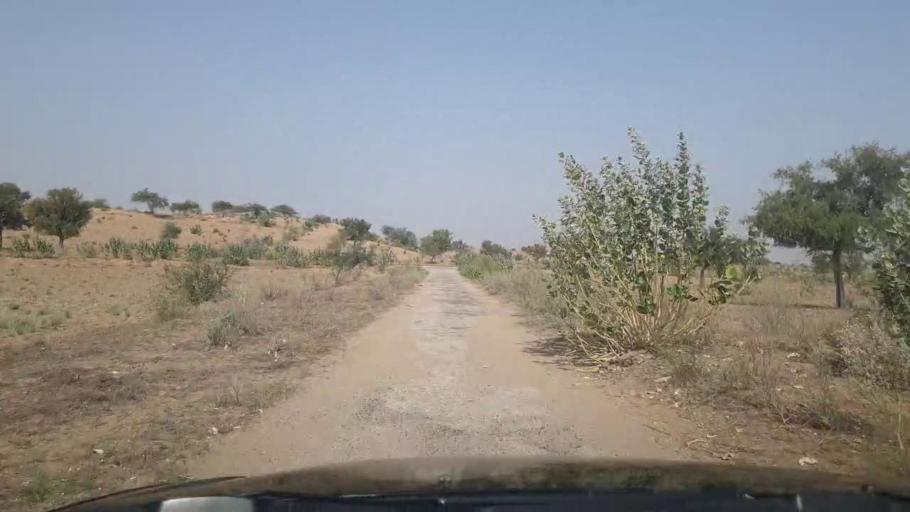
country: PK
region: Sindh
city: Islamkot
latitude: 25.0638
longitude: 70.2040
